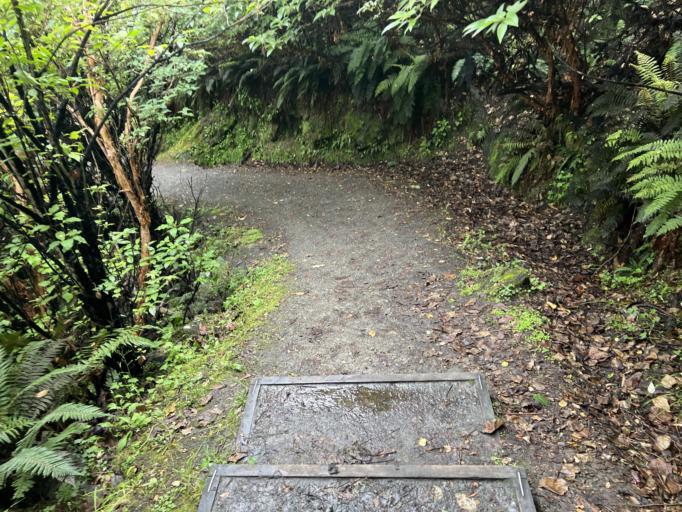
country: NZ
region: Otago
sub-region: Queenstown-Lakes District
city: Wanaka
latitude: -44.6461
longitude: 168.9630
